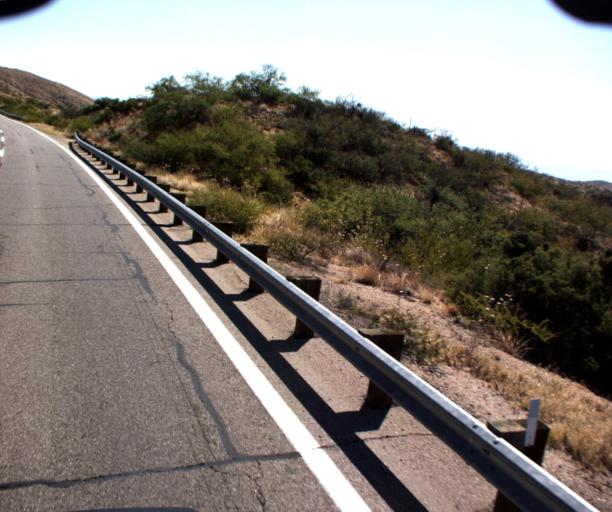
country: US
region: Arizona
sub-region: Pinal County
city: Oracle
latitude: 32.6340
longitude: -110.7355
